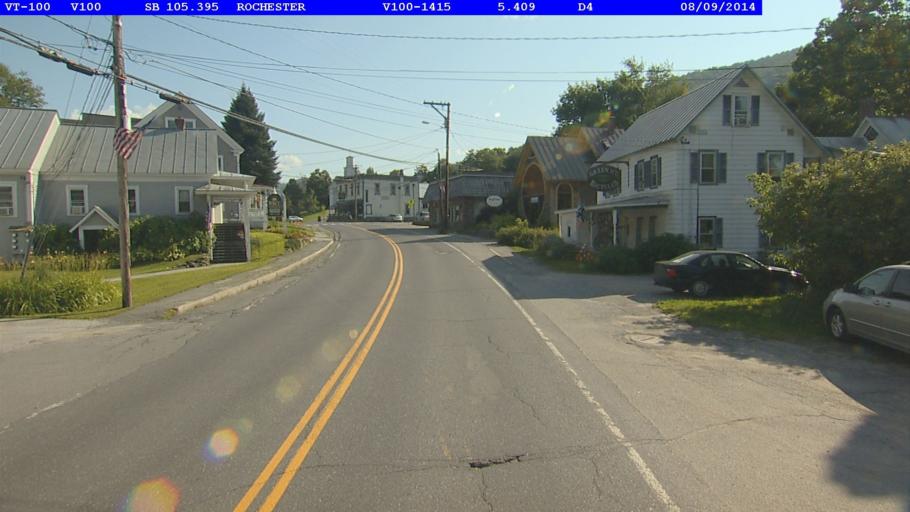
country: US
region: Vermont
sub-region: Orange County
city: Randolph
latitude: 43.8762
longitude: -72.8081
